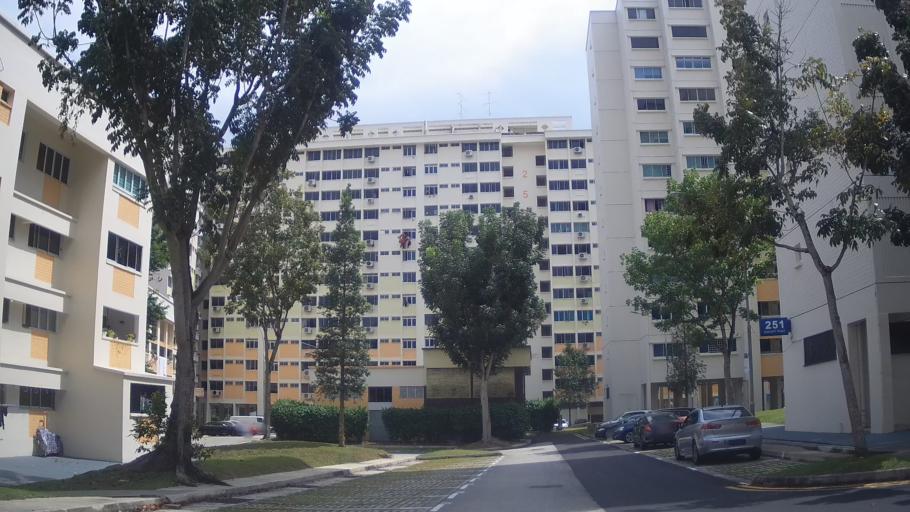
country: MY
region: Johor
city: Johor Bahru
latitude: 1.3806
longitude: 103.7743
